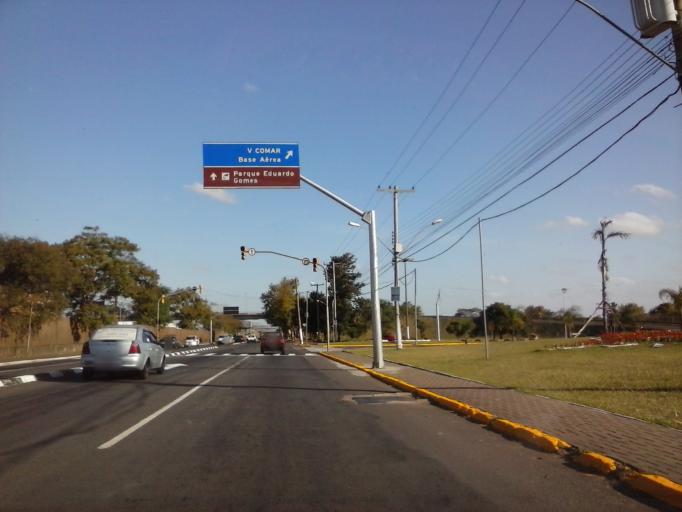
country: BR
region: Rio Grande do Sul
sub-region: Canoas
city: Canoas
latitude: -29.9342
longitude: -51.1778
